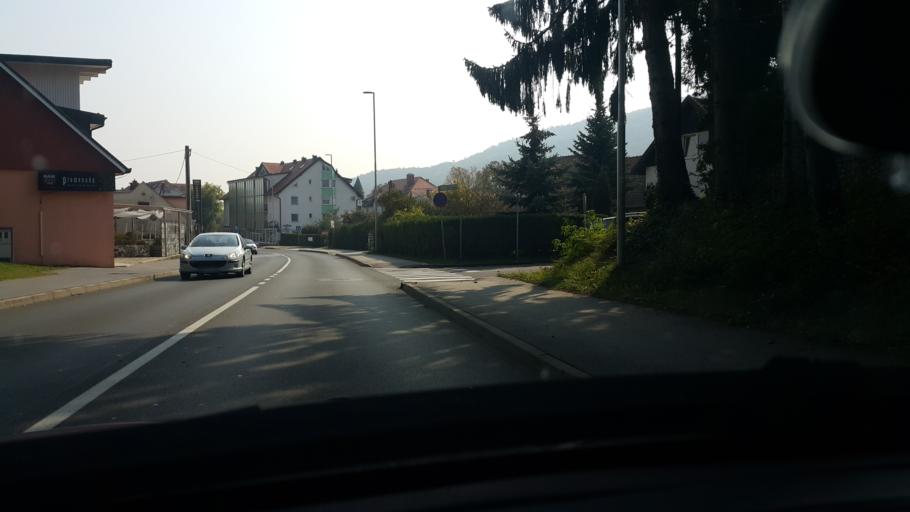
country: SI
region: Maribor
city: Pekre
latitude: 46.5392
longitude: 15.6101
